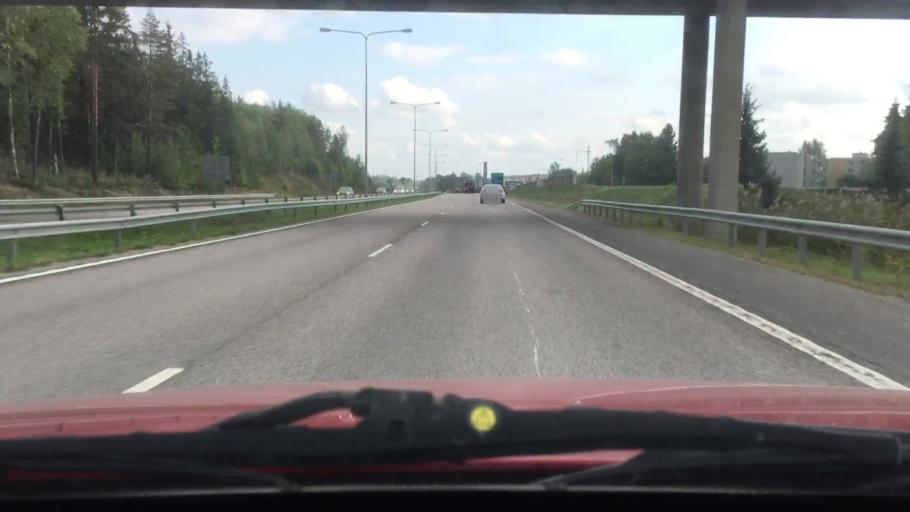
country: FI
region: Varsinais-Suomi
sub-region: Turku
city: Raisio
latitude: 60.4959
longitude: 22.1652
